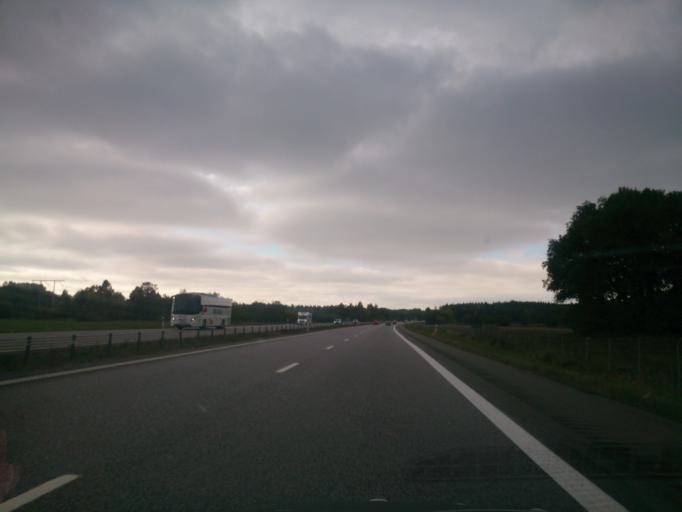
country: SE
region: OEstergoetland
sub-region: Linkopings Kommun
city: Linghem
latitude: 58.4621
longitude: 15.7937
